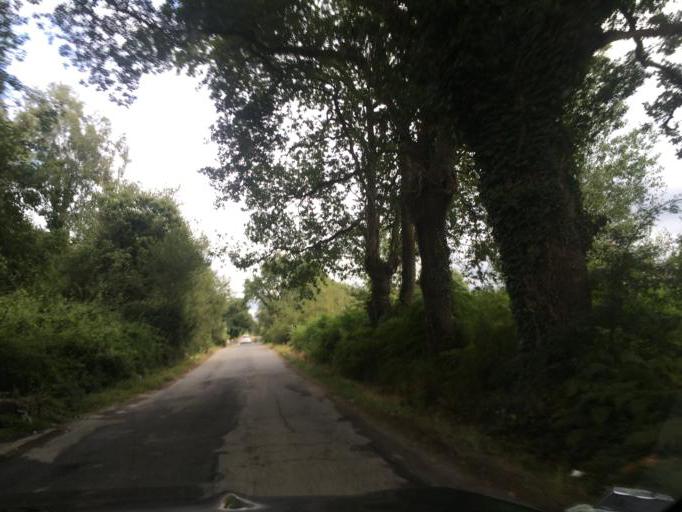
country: FR
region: Aquitaine
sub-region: Departement des Pyrenees-Atlantiques
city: Buros
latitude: 43.3169
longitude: -0.2982
